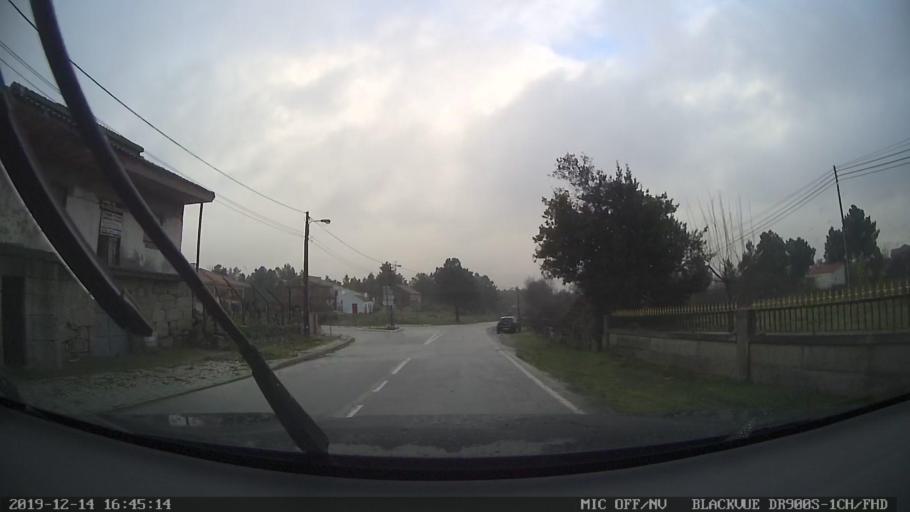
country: PT
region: Vila Real
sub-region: Murca
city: Murca
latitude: 41.3983
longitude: -7.4877
